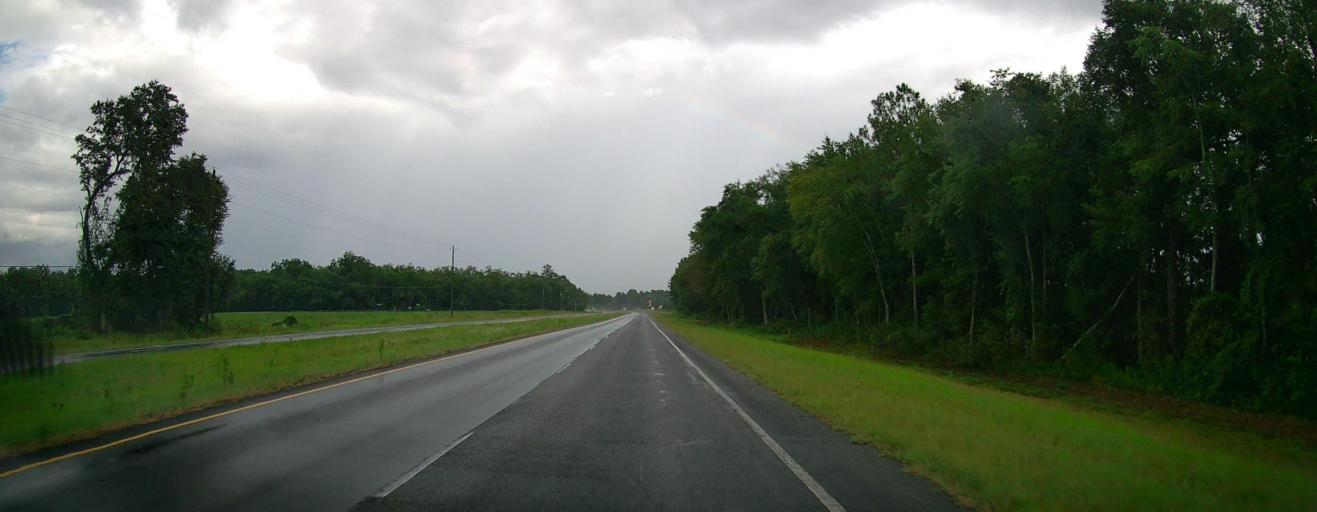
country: US
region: Georgia
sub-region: Ware County
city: Deenwood
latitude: 31.2556
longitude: -82.4869
